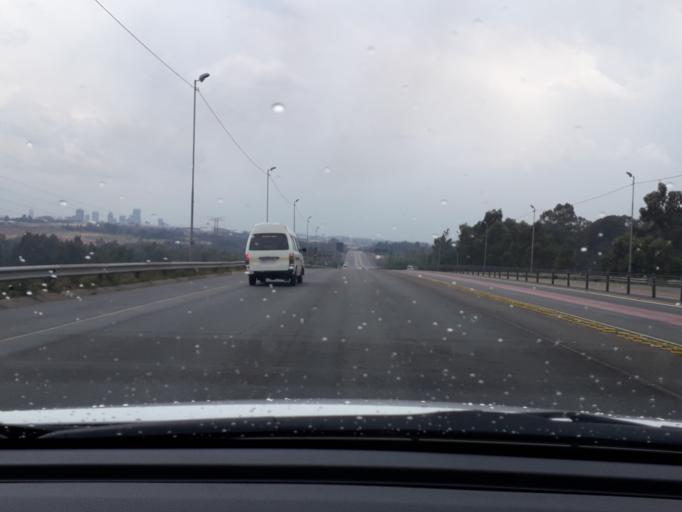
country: ZA
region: Gauteng
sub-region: City of Johannesburg Metropolitan Municipality
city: Johannesburg
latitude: -26.2308
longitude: 27.9857
